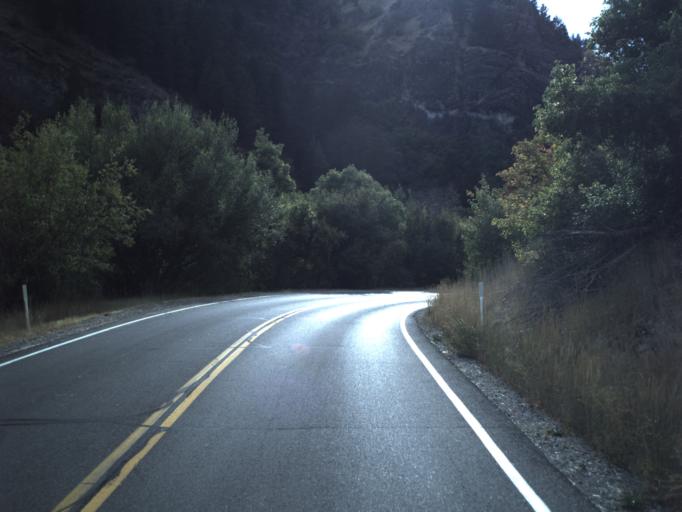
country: US
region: Utah
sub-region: Cache County
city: Millville
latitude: 41.6289
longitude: -111.6943
